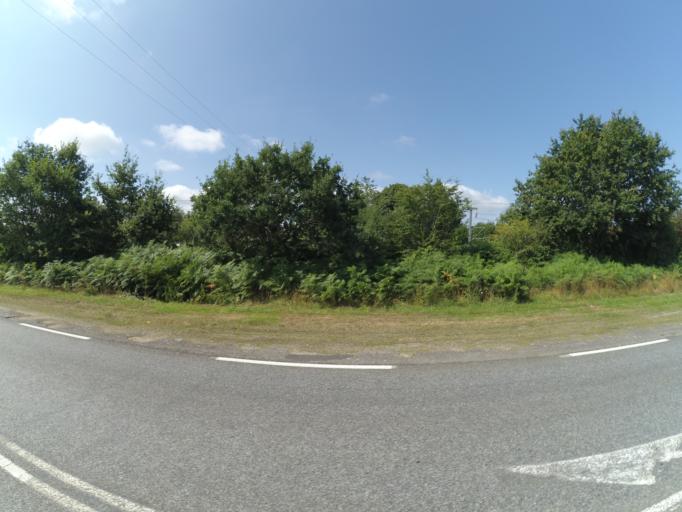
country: FR
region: Brittany
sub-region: Departement du Finistere
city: Bannalec
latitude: 47.9348
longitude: -3.7171
